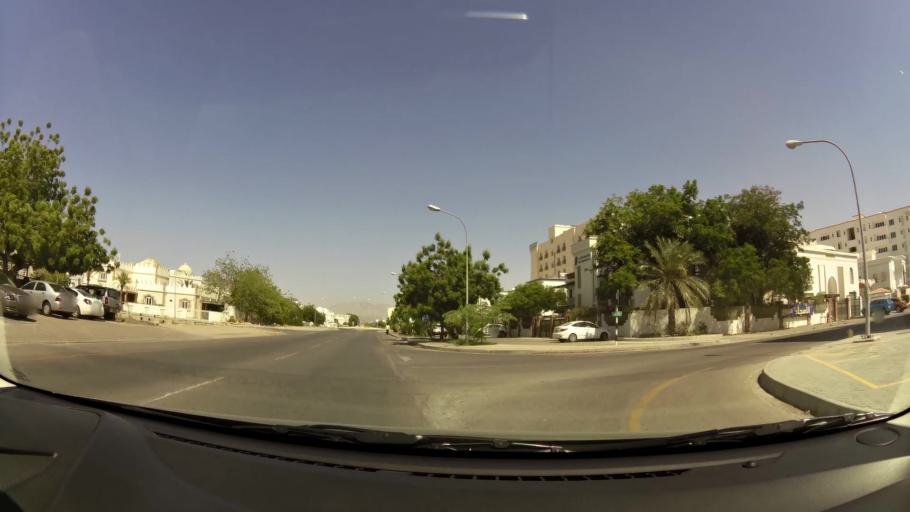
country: OM
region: Muhafazat Masqat
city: Bawshar
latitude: 23.5956
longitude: 58.3631
